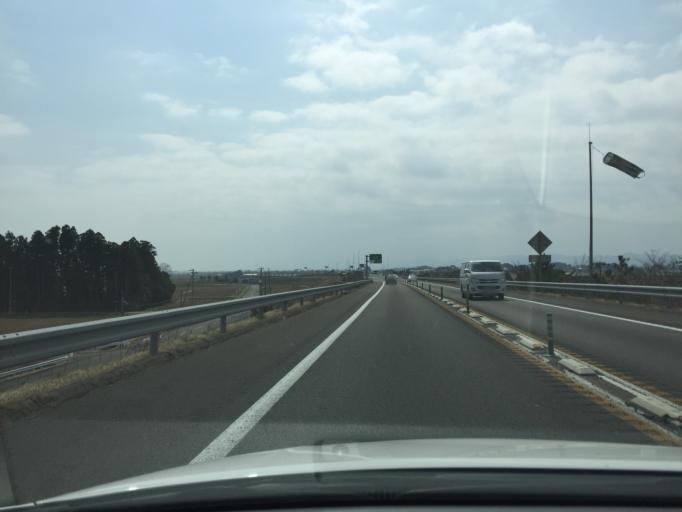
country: JP
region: Miyagi
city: Iwanuma
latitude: 38.0915
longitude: 140.8873
